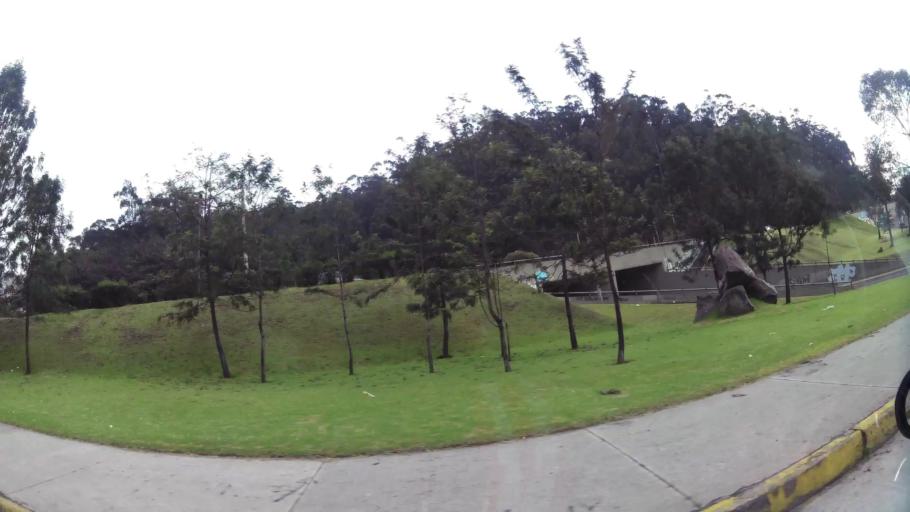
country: EC
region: Pichincha
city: Quito
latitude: -0.2067
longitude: -78.5119
